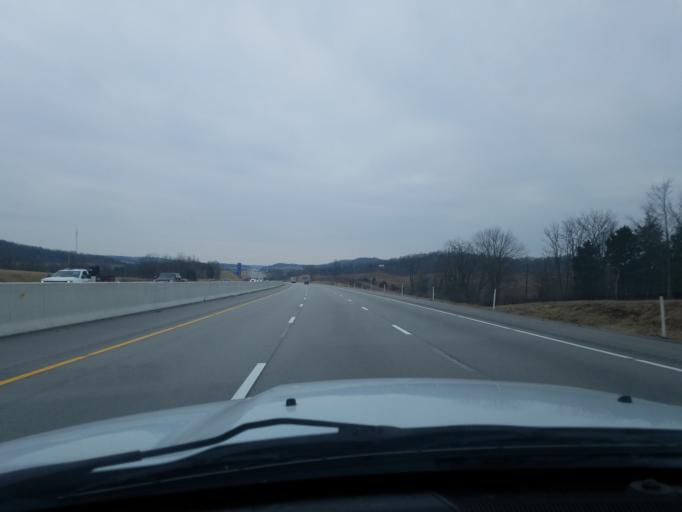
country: US
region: Kentucky
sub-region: Hart County
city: Munfordville
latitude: 37.2626
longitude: -85.9221
